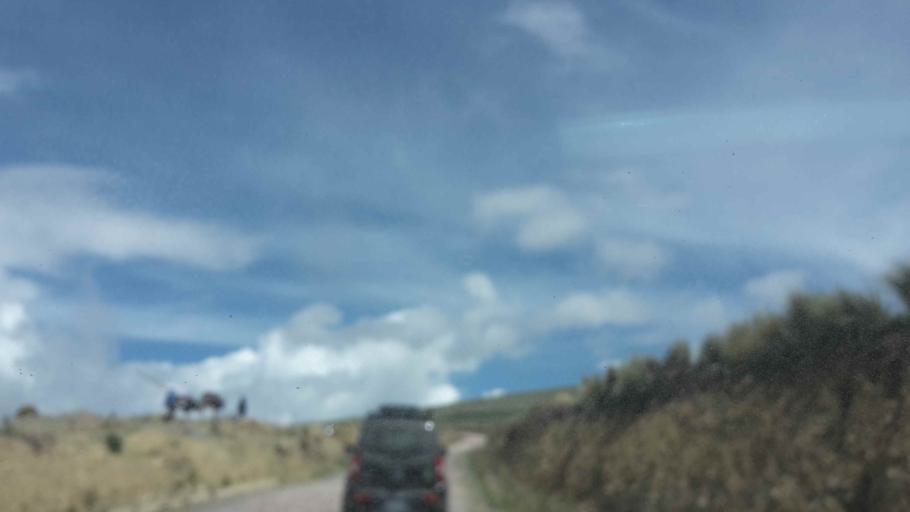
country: BO
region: Cochabamba
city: Cochabamba
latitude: -17.3167
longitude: -66.0795
